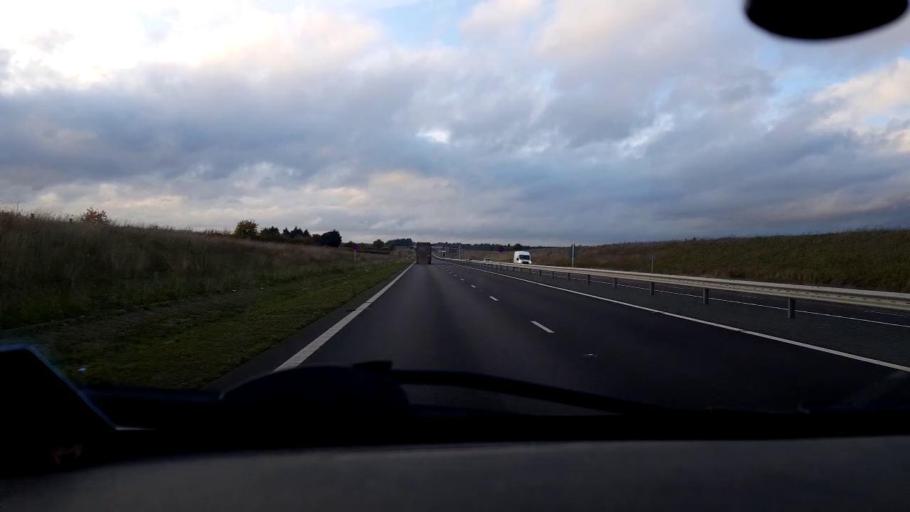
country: GB
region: England
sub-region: Norfolk
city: Horsford
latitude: 52.6884
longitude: 1.2365
